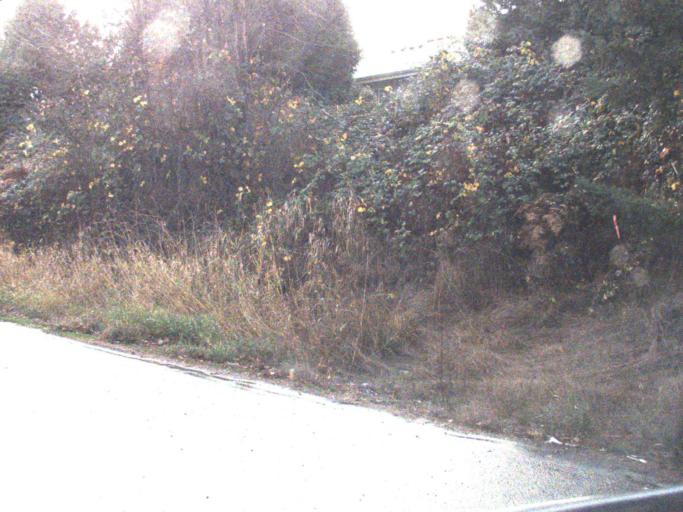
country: US
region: Washington
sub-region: Snohomish County
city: West Lake Stevens
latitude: 47.9970
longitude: -122.1054
